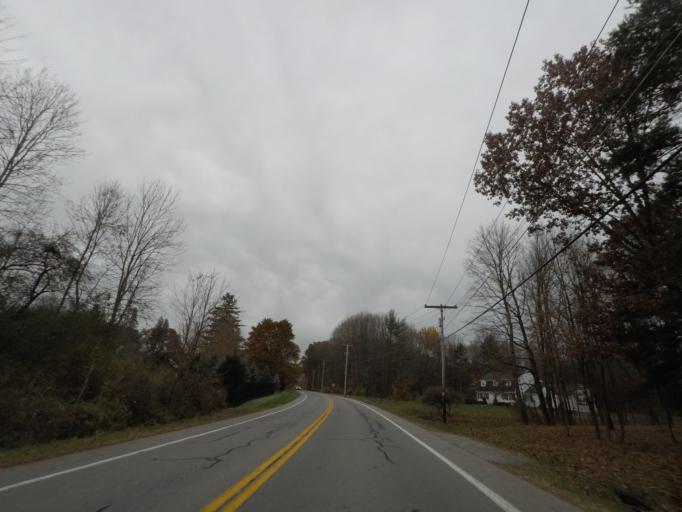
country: US
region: New York
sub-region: Schenectady County
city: Niskayuna
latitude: 42.8135
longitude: -73.8268
